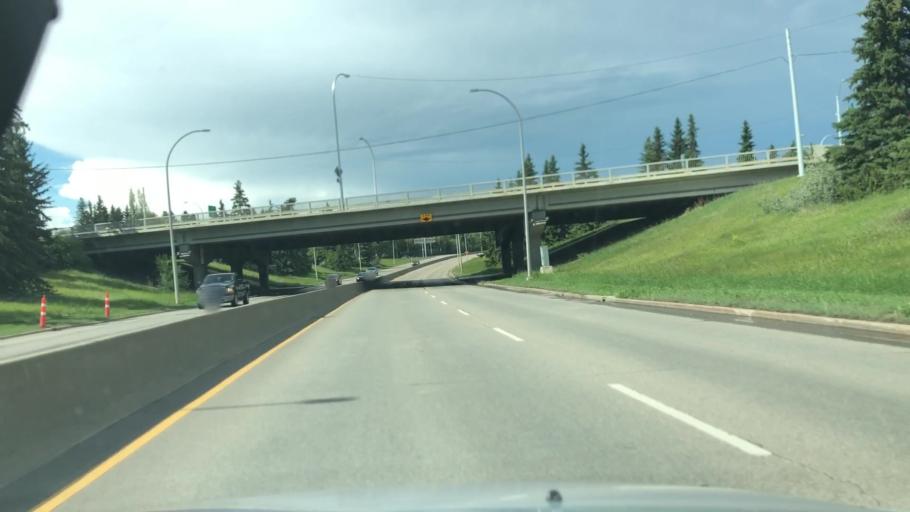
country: CA
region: Alberta
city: Edmonton
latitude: 53.5503
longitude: -113.5494
